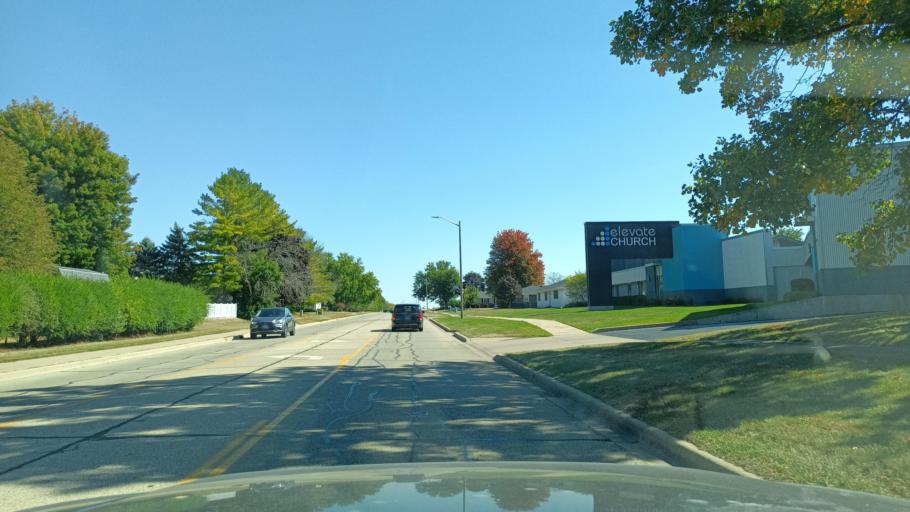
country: US
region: Illinois
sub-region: Tazewell County
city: Morton
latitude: 40.6131
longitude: -89.4433
